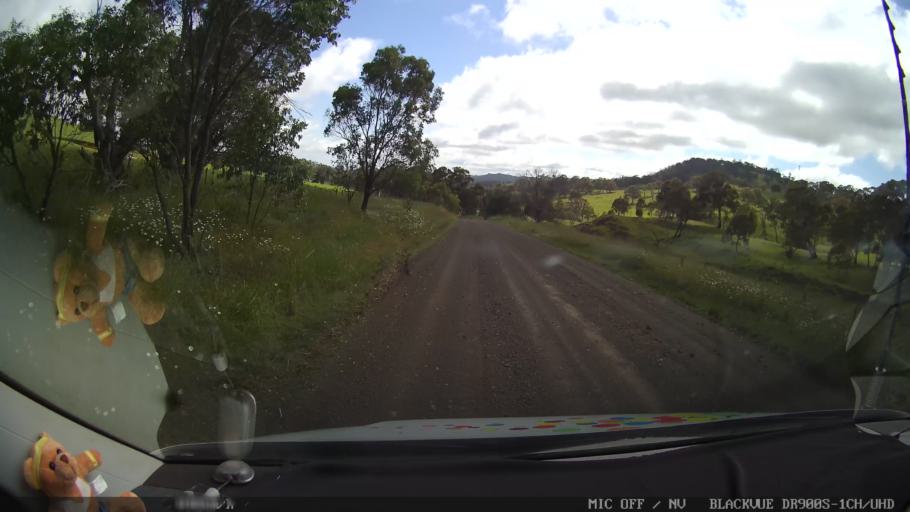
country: AU
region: New South Wales
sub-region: Guyra
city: Guyra
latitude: -30.0065
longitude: 151.6666
